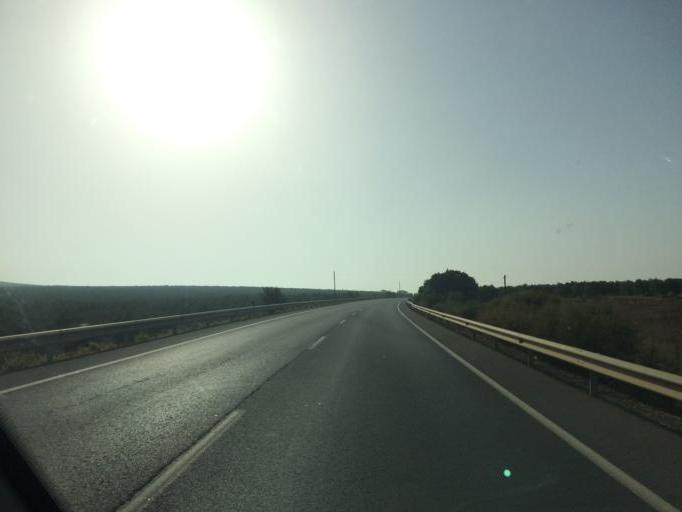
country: ES
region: Andalusia
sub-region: Provincia de Malaga
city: Humilladero
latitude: 37.0586
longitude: -4.6837
